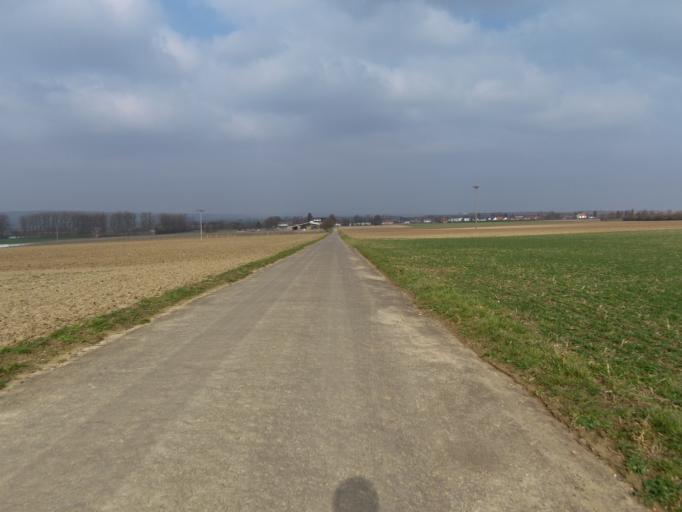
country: DE
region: Rheinland-Pfalz
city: Obersulzen
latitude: 49.5585
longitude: 8.2109
